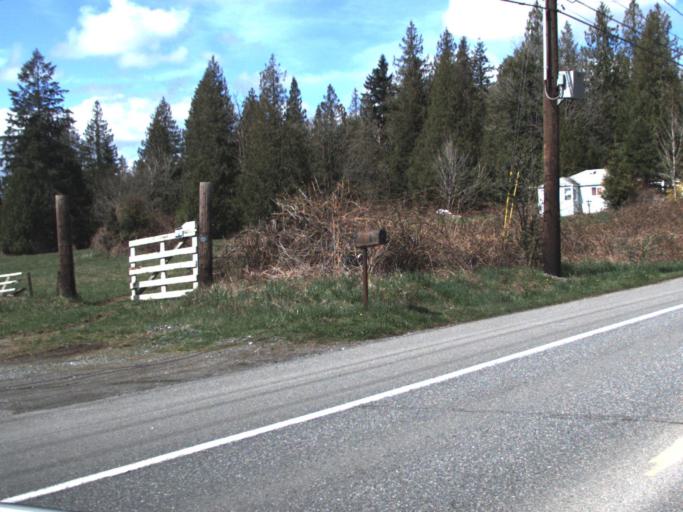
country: US
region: Washington
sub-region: King County
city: Black Diamond
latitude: 47.3231
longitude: -122.0071
